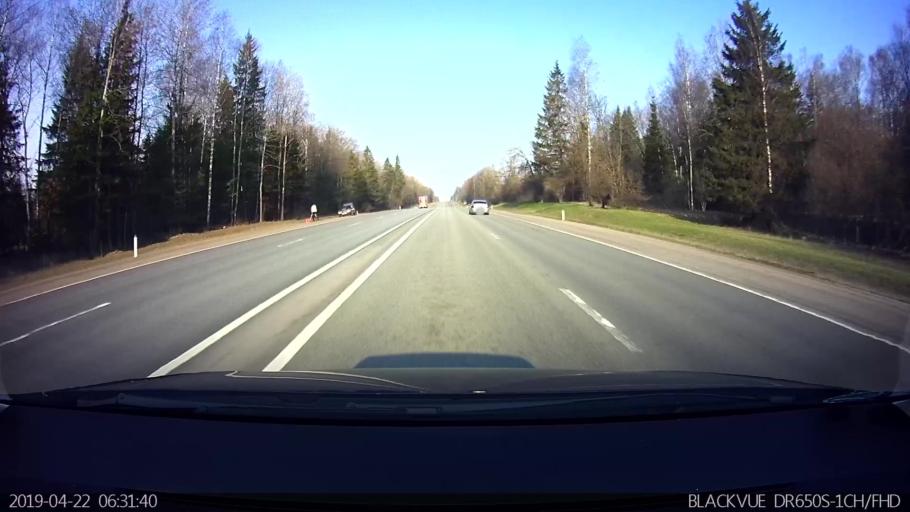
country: RU
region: Moskovskaya
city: Uvarovka
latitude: 55.4679
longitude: 35.5732
